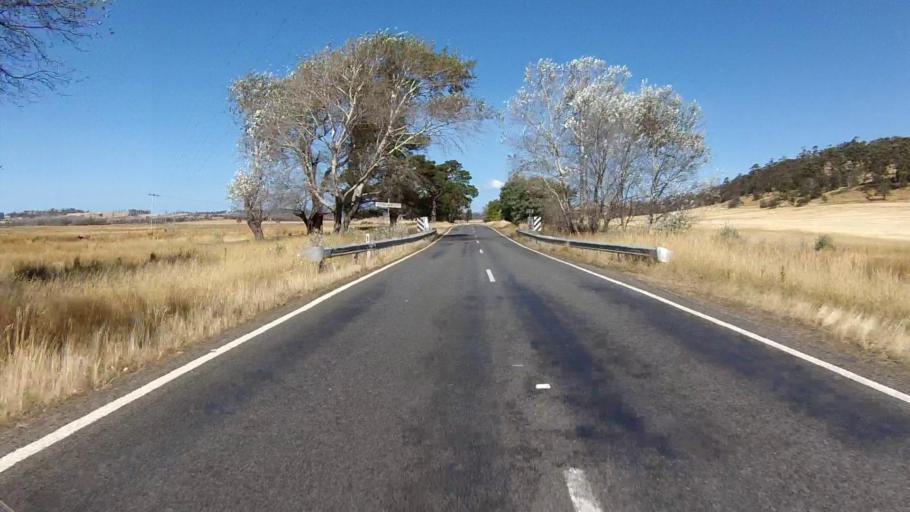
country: AU
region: Tasmania
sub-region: Sorell
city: Sorell
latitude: -42.4736
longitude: 147.9270
